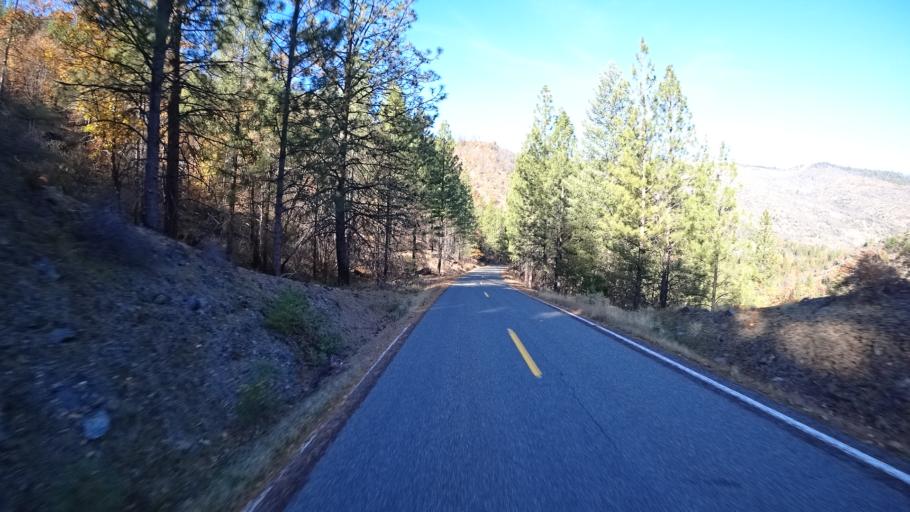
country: US
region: California
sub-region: Siskiyou County
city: Yreka
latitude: 41.9061
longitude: -122.8326
